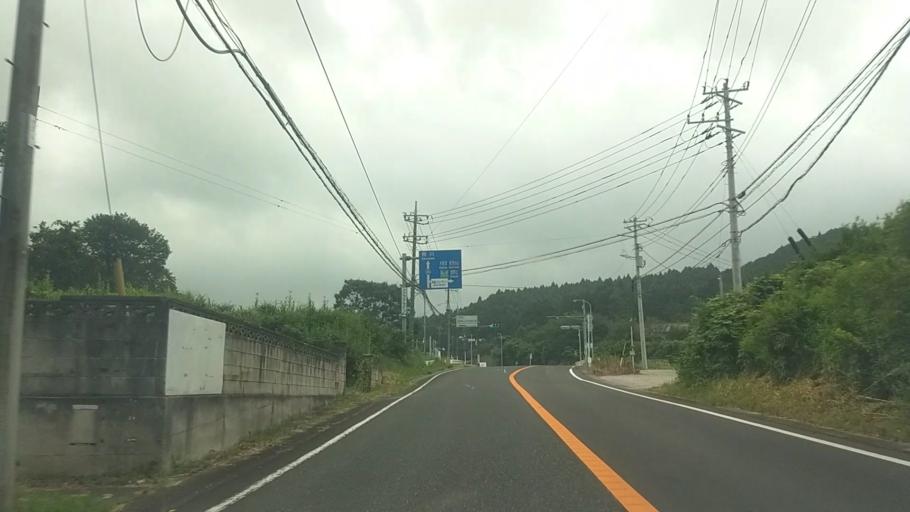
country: JP
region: Chiba
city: Kawaguchi
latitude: 35.2062
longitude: 140.0709
